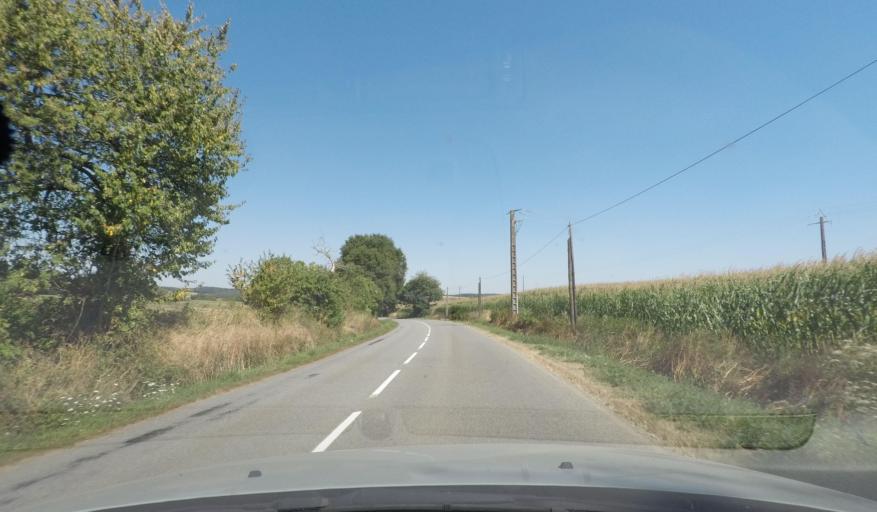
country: FR
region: Brittany
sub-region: Departement du Morbihan
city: Caro
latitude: 47.8348
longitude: -2.3253
